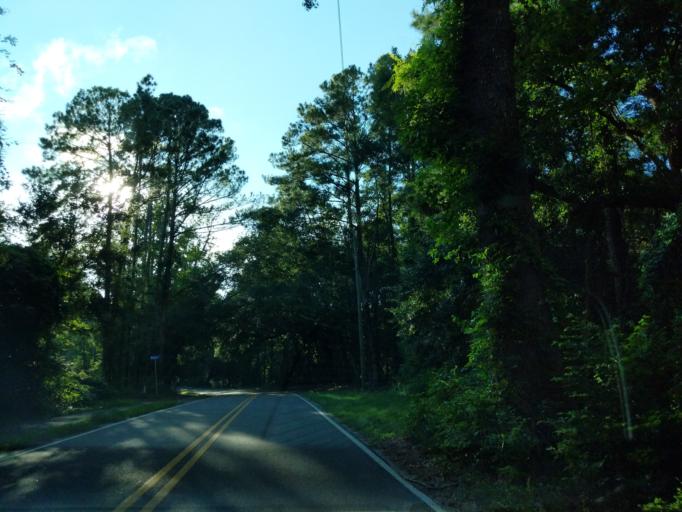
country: US
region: South Carolina
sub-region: Charleston County
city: Awendaw
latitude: 33.0937
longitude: -79.4676
